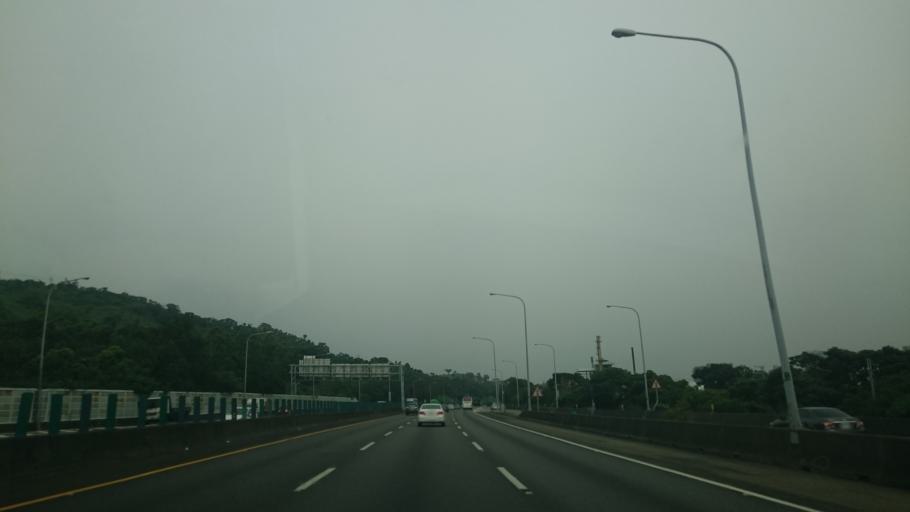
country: TW
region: Taiwan
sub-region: Changhua
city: Chang-hua
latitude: 24.1183
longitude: 120.5862
